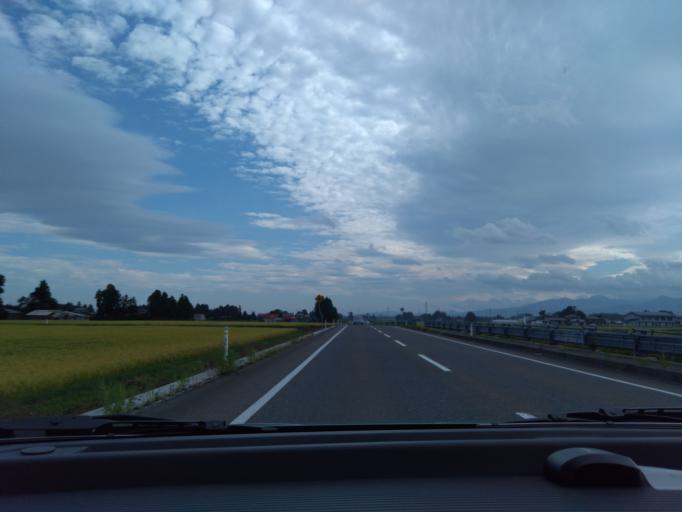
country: JP
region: Iwate
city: Hanamaki
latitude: 39.3607
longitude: 141.0557
